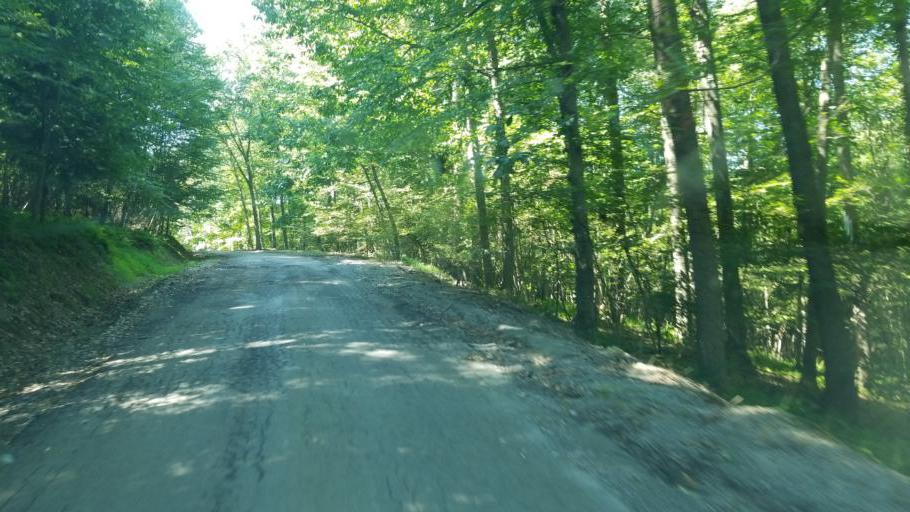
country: US
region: Pennsylvania
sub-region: Clarion County
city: Marianne
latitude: 41.1913
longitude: -79.4412
